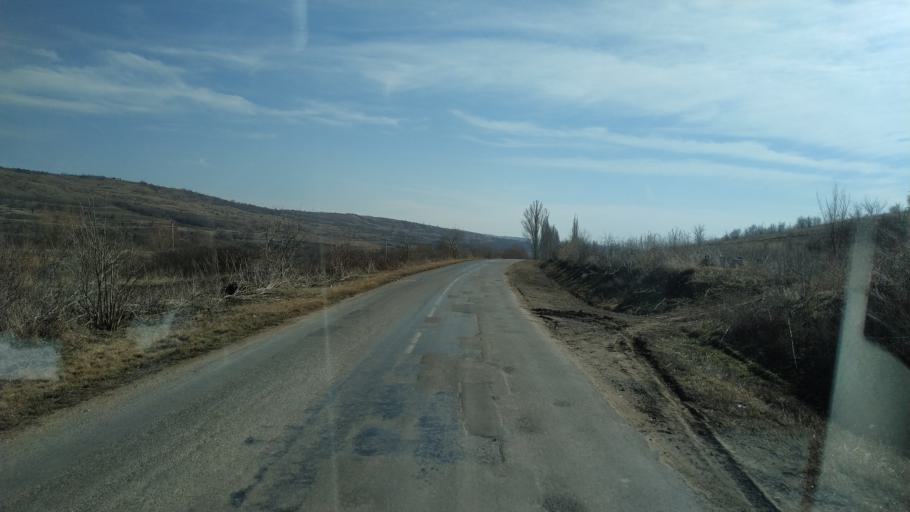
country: MD
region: Nisporeni
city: Nisporeni
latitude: 47.1665
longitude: 28.0986
